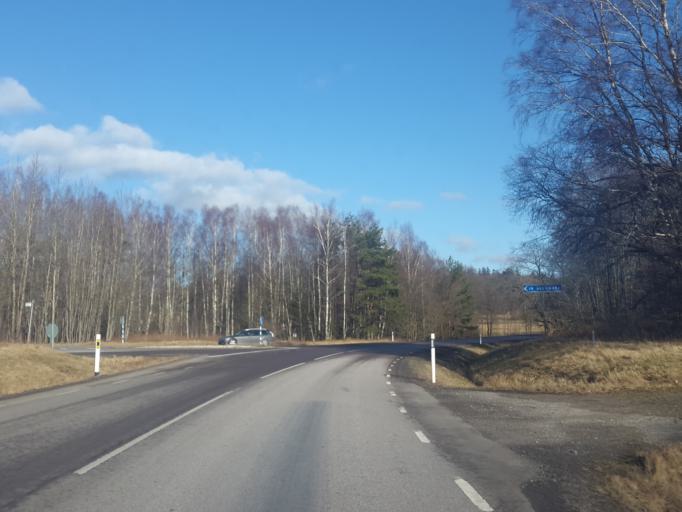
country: SE
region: Vaestra Goetaland
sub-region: Lerums Kommun
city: Grabo
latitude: 57.9171
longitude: 12.3423
